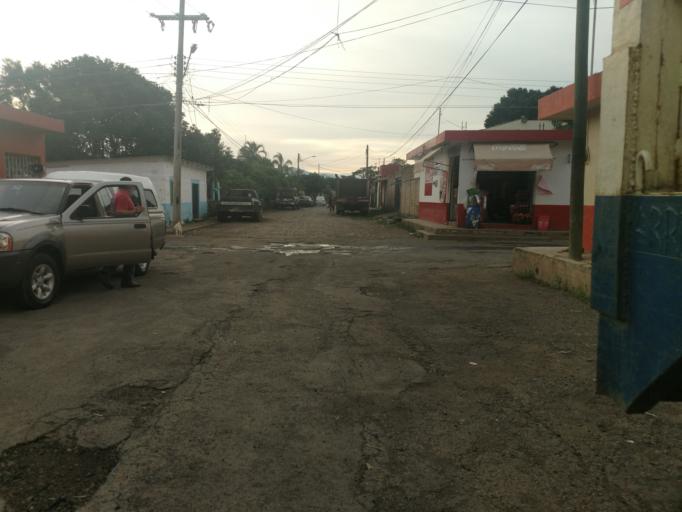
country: MX
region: Nayarit
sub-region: Tepic
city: La Corregidora
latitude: 21.4633
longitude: -104.8028
